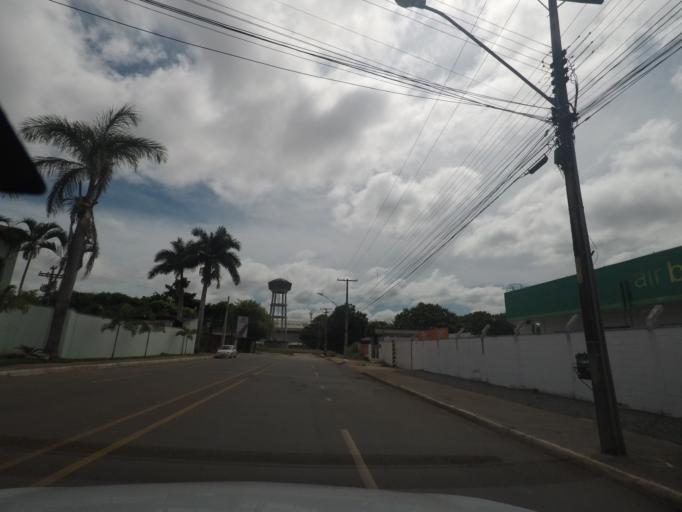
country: BR
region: Goias
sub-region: Goiania
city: Goiania
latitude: -16.6352
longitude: -49.2276
